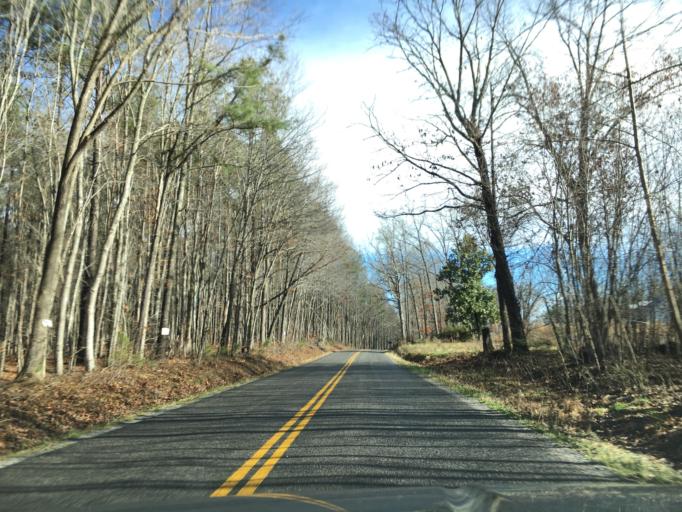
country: US
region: Virginia
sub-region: Amelia County
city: Amelia Court House
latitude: 37.4361
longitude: -78.0413
